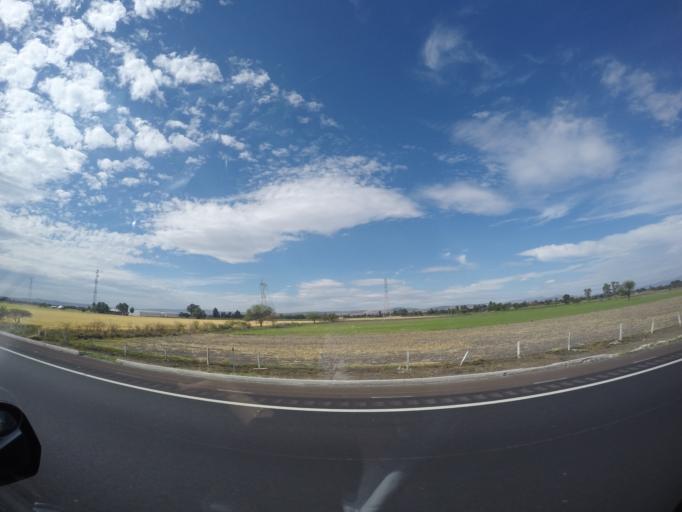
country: MX
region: Guanajuato
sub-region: Santa Cruz de Juventino Rosas
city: Franco Tavera
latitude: 20.5722
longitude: -100.9060
